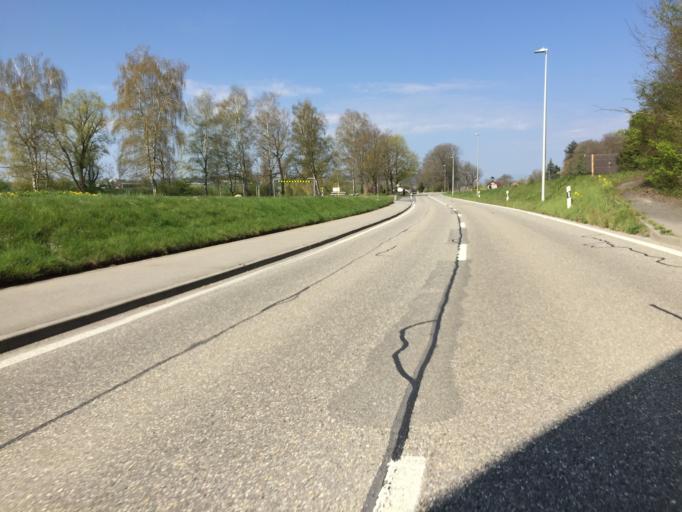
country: CH
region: Bern
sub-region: Bern-Mittelland District
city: Urtenen
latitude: 47.0233
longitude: 7.4862
